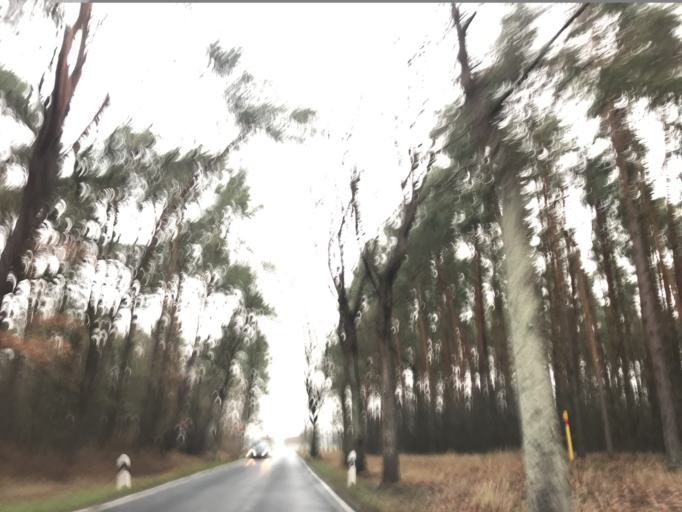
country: DE
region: Brandenburg
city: Brieselang
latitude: 52.6645
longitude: 12.9797
